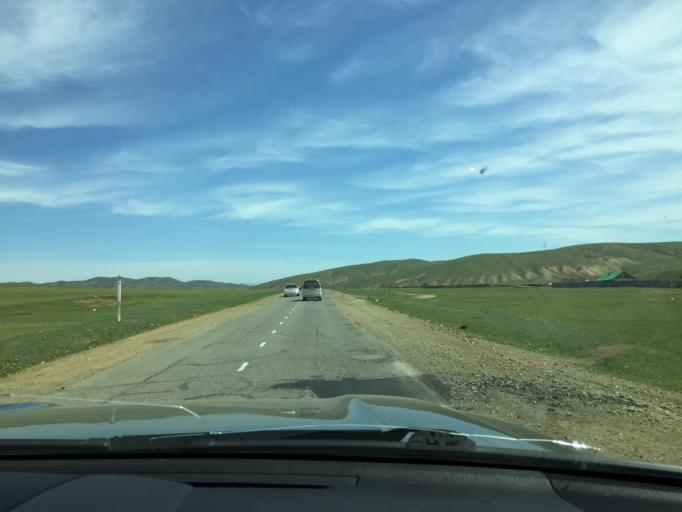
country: MN
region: Central Aimak
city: Bornuur
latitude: 48.6644
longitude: 106.1278
